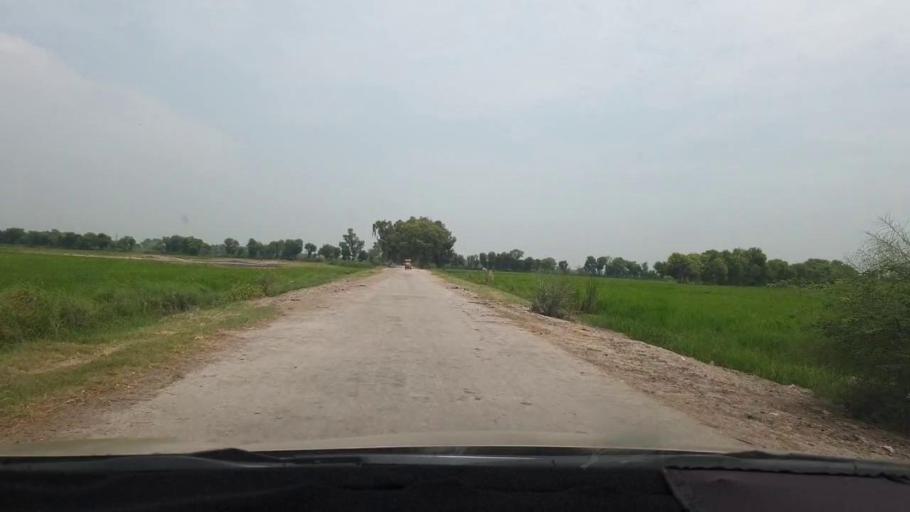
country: PK
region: Sindh
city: Ratodero
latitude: 27.7578
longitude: 68.3163
